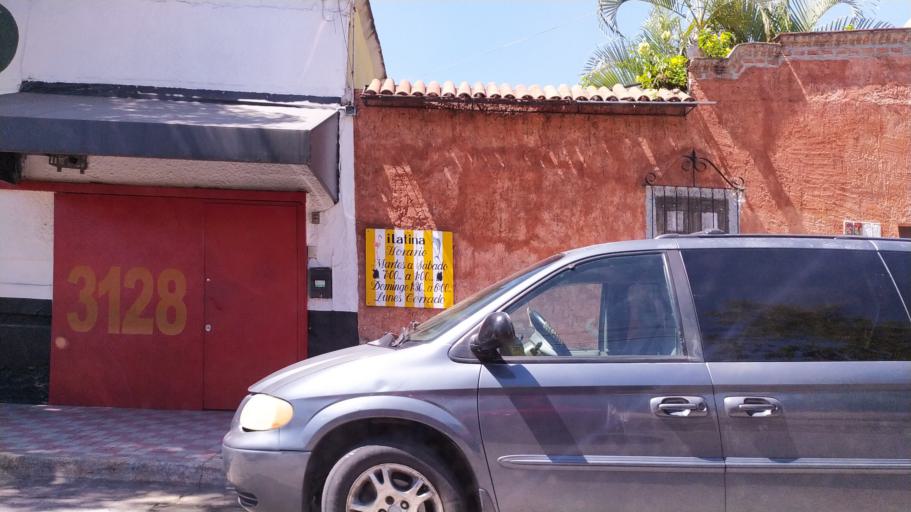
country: MX
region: Jalisco
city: Guadalajara
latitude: 20.6719
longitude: -103.3923
